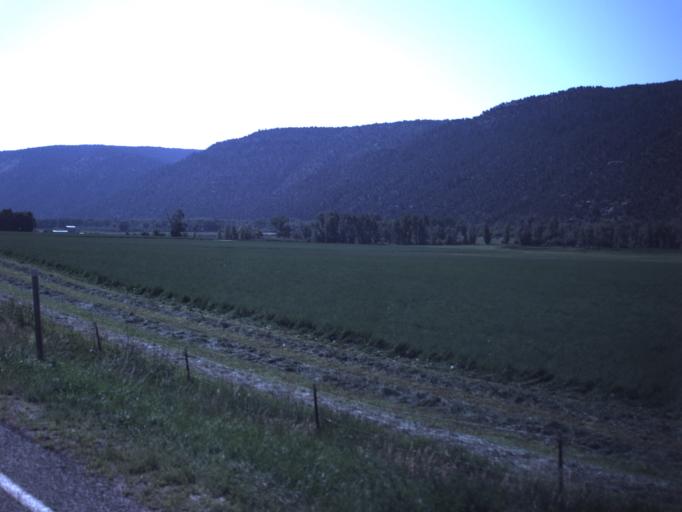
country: US
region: Utah
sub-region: Duchesne County
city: Duchesne
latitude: 40.3165
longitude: -110.6485
